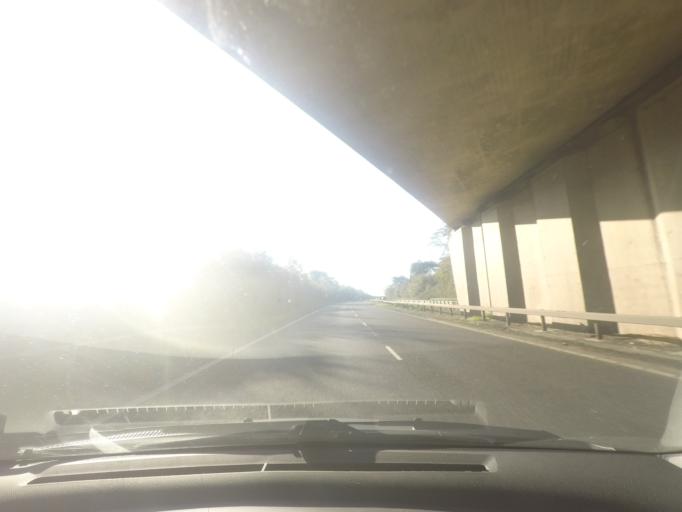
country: GB
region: England
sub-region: North Lincolnshire
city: Barton upon Humber
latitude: 53.6632
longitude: -0.4485
